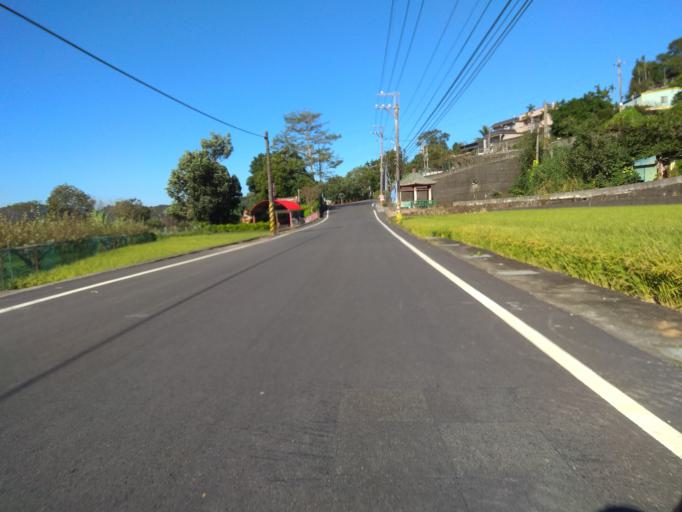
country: TW
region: Taiwan
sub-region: Hsinchu
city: Zhubei
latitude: 24.8451
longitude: 121.1215
